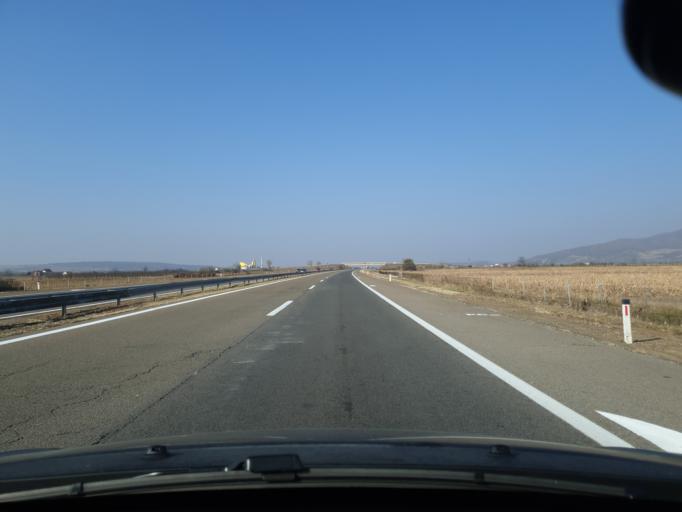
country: RS
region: Central Serbia
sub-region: Nisavski Okrug
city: Doljevac
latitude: 43.1686
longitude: 21.8753
